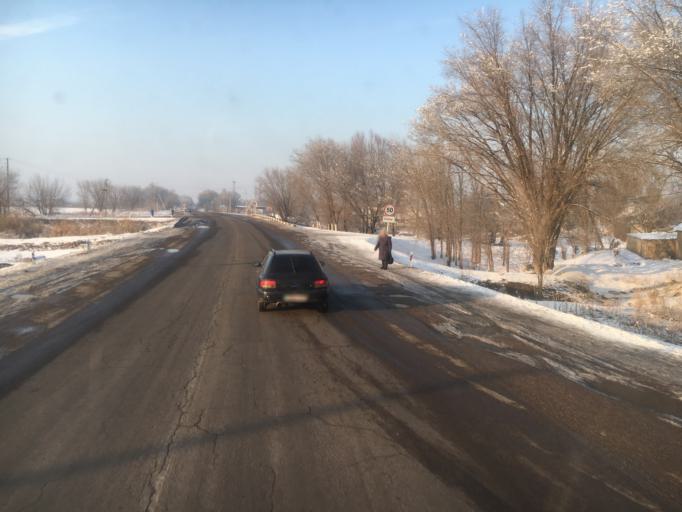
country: KZ
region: Almaty Oblysy
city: Burunday
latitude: 43.3314
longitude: 76.6619
